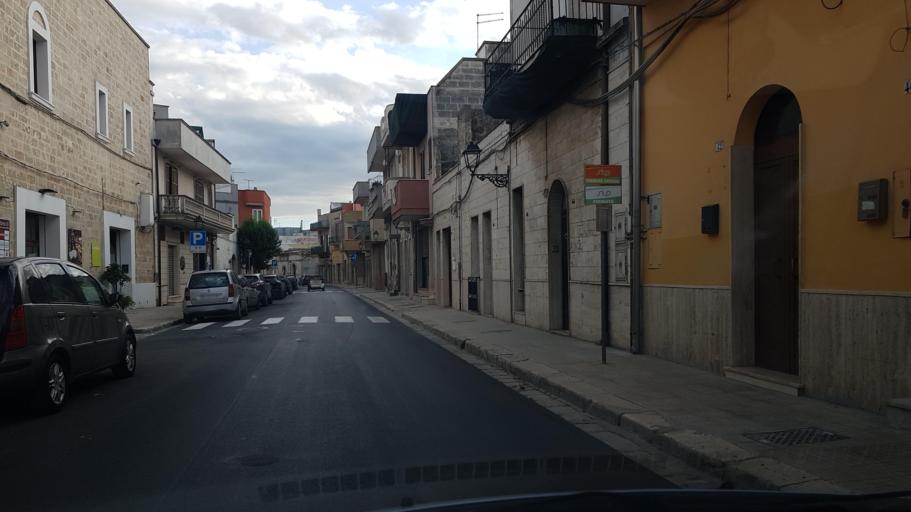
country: IT
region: Apulia
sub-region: Provincia di Brindisi
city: Francavilla Fontana
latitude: 40.5330
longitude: 17.5782
